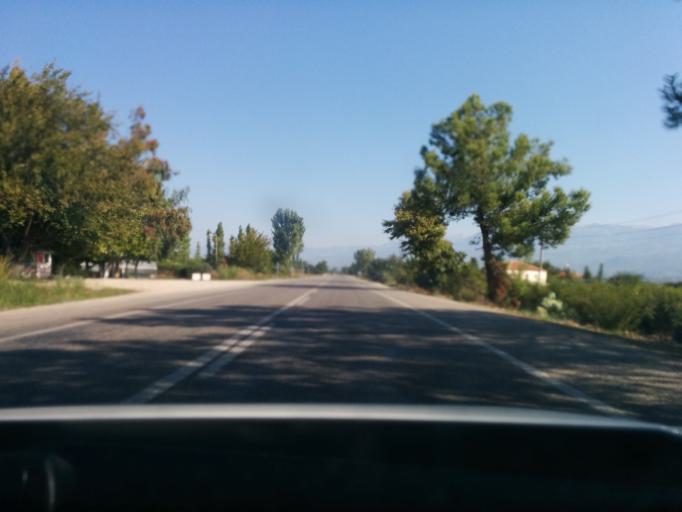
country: TR
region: Mugla
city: Esen
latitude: 36.5079
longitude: 29.3320
